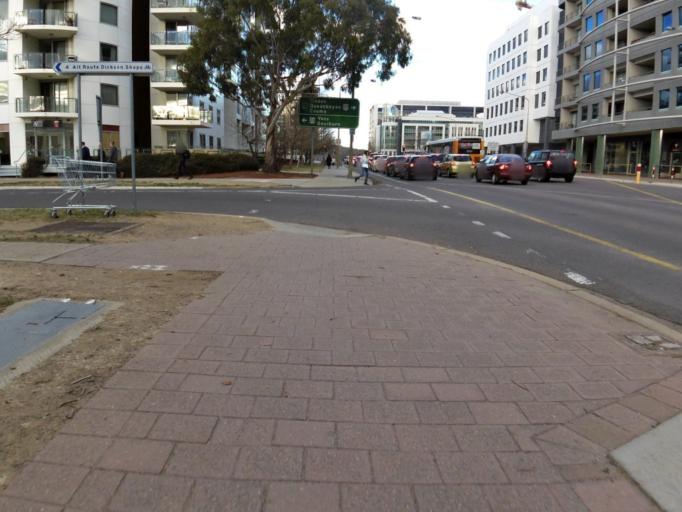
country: AU
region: Australian Capital Territory
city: Canberra
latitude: -35.2755
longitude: 149.1281
